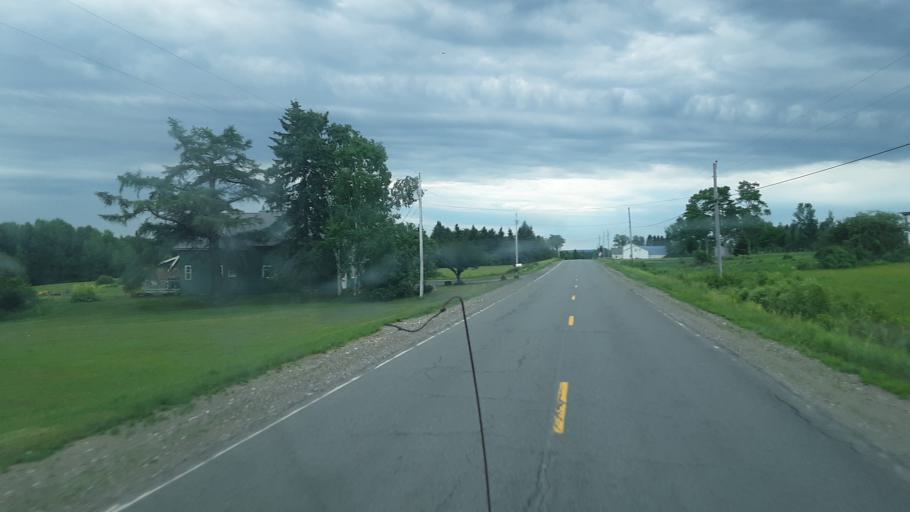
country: US
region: Maine
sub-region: Penobscot County
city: Patten
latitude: 45.8029
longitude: -68.3251
